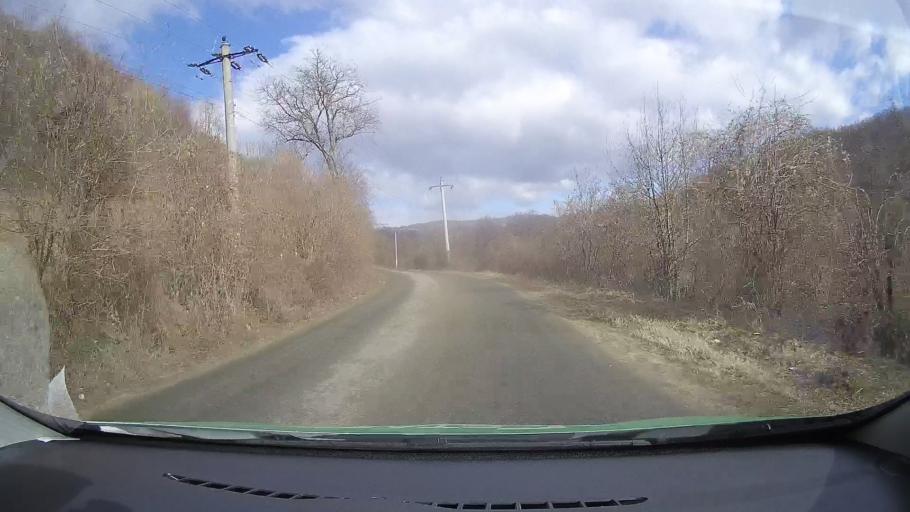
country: RO
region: Dambovita
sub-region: Comuna Motaeni
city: Motaeni
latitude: 45.1064
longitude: 25.4423
